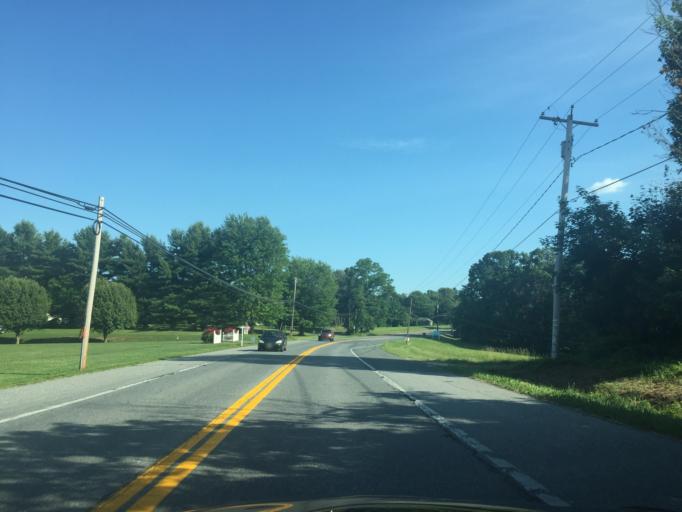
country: US
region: Maryland
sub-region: Harford County
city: Jarrettsville
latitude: 39.6386
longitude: -76.4709
